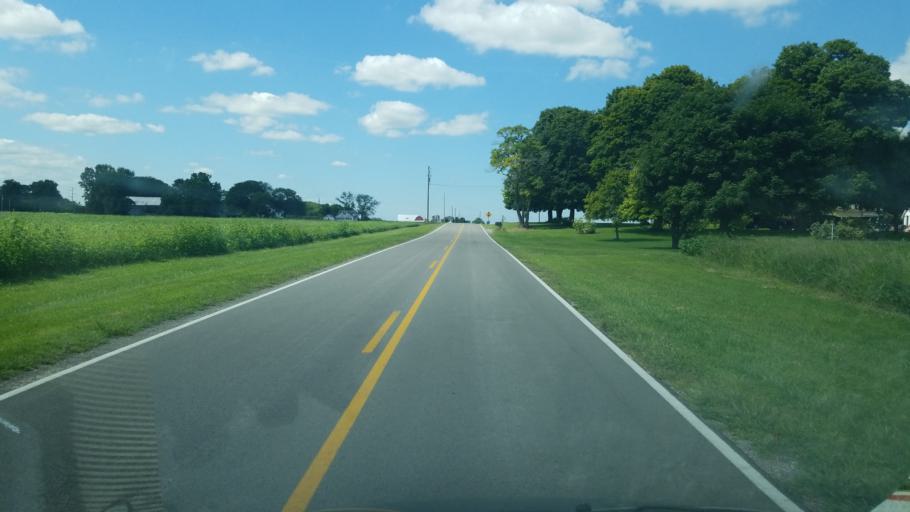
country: US
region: Ohio
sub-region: Fulton County
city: Delta
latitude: 41.6032
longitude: -83.9649
